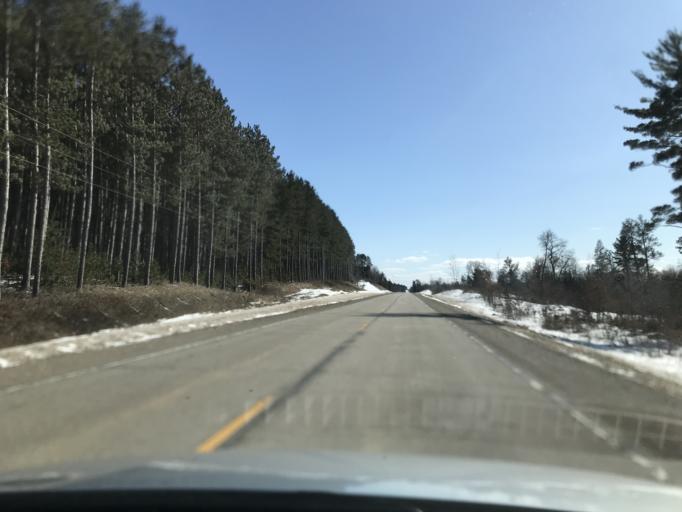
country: US
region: Wisconsin
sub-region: Marinette County
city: Niagara
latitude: 45.3811
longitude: -88.0999
